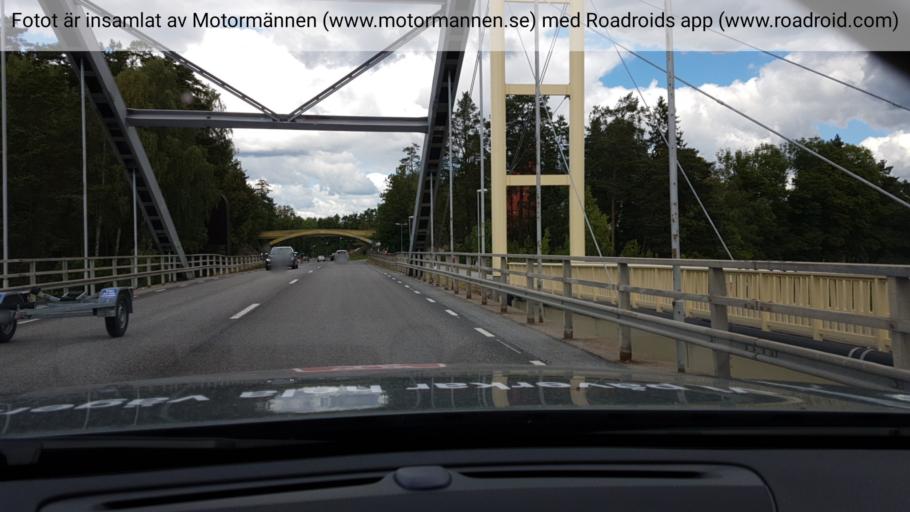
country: SE
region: Stockholm
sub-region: Vaxholms Kommun
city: Resaro
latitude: 59.4102
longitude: 18.3167
